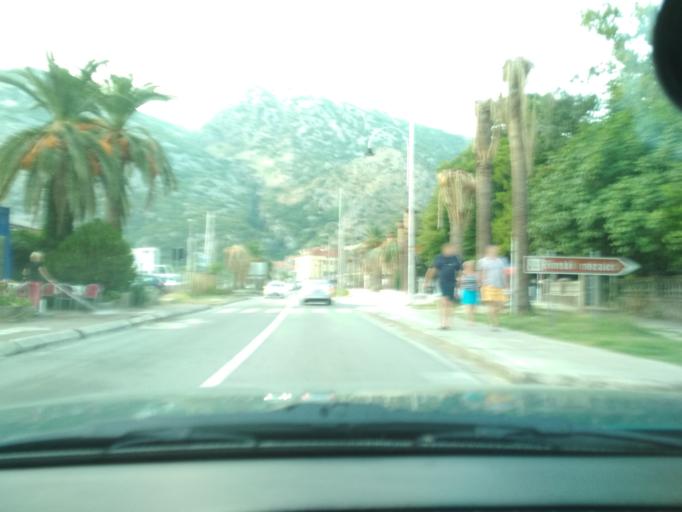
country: ME
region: Kotor
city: Risan
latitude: 42.5133
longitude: 18.6950
